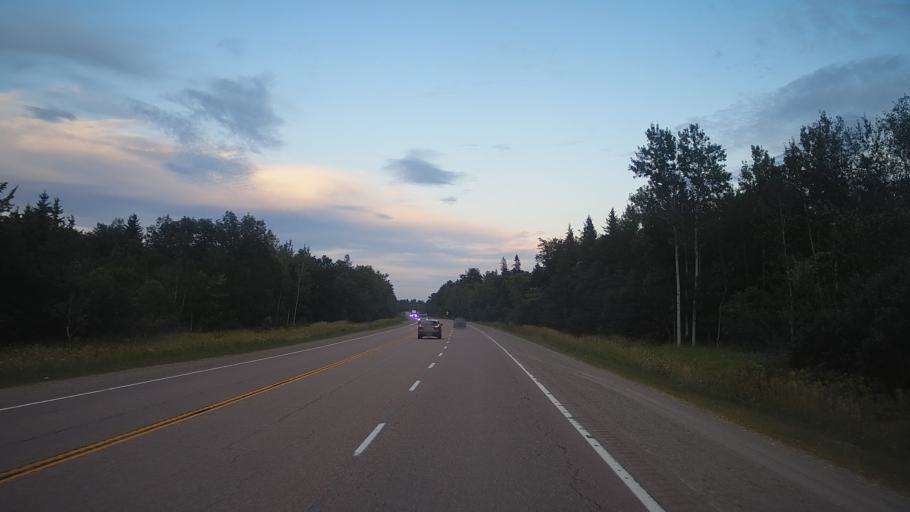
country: CA
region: Ontario
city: Pembroke
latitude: 45.7605
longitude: -77.0535
